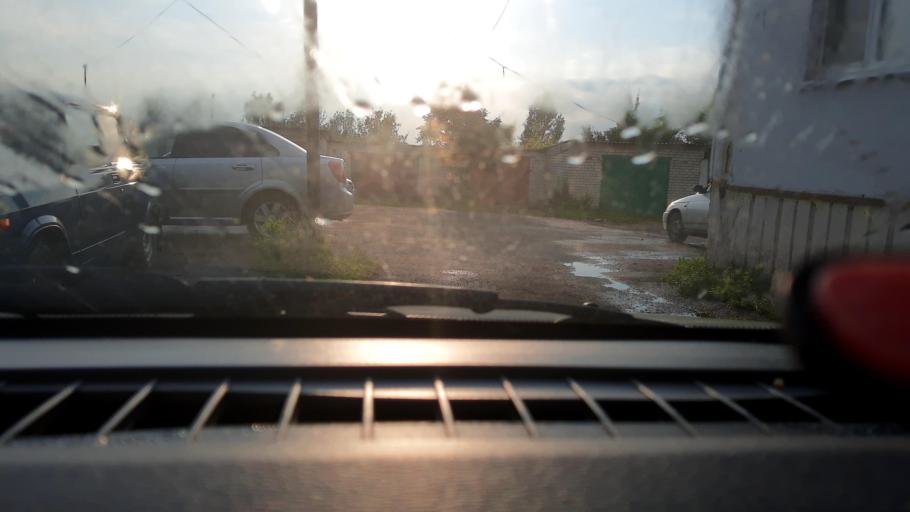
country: RU
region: Nizjnij Novgorod
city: Lukoyanov
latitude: 55.0449
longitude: 44.4938
